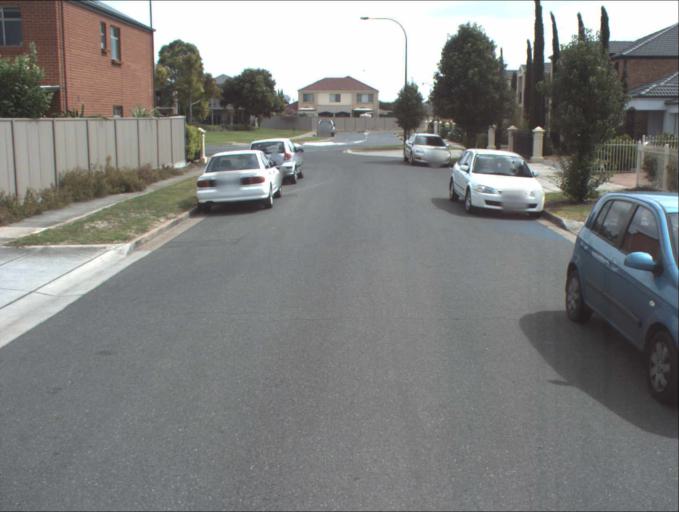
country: AU
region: South Australia
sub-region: Charles Sturt
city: Woodville
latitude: -34.8742
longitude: 138.5617
